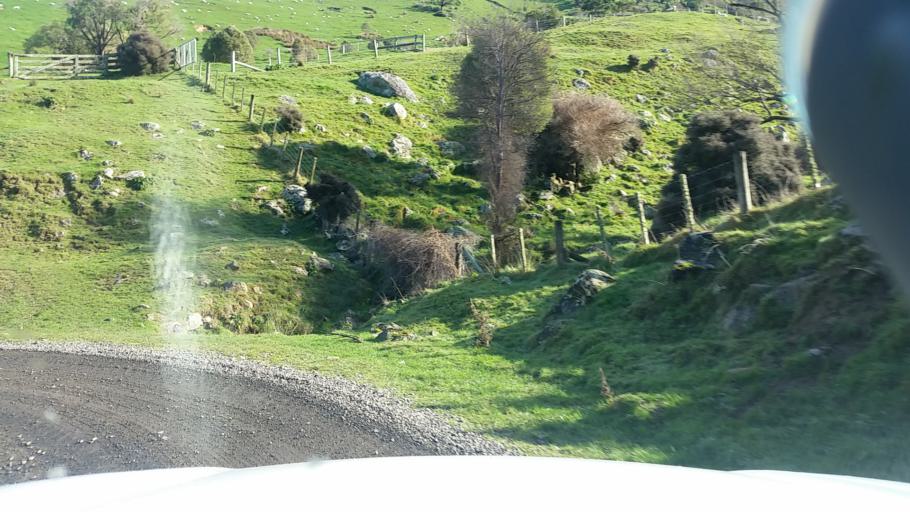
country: NZ
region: Canterbury
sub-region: Christchurch City
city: Christchurch
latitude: -43.6660
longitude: 172.8702
